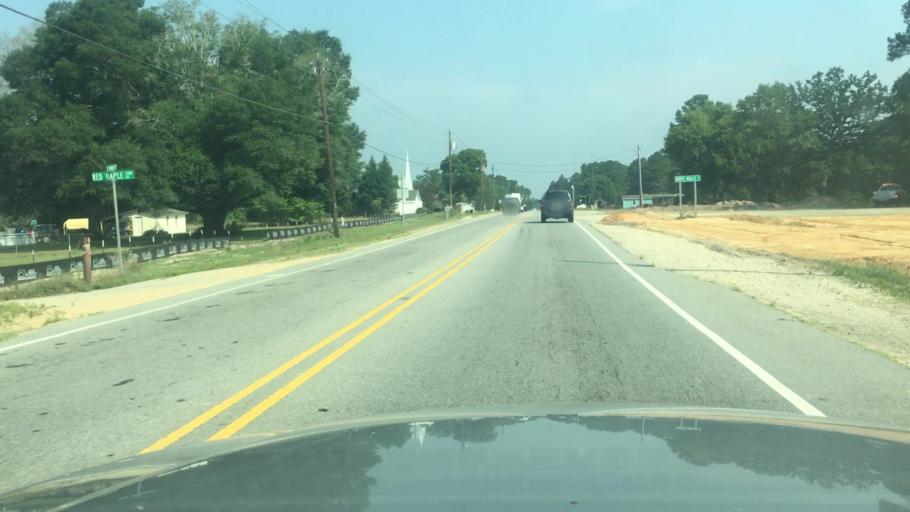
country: US
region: North Carolina
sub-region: Cumberland County
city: Hope Mills
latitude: 34.9469
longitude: -78.9327
